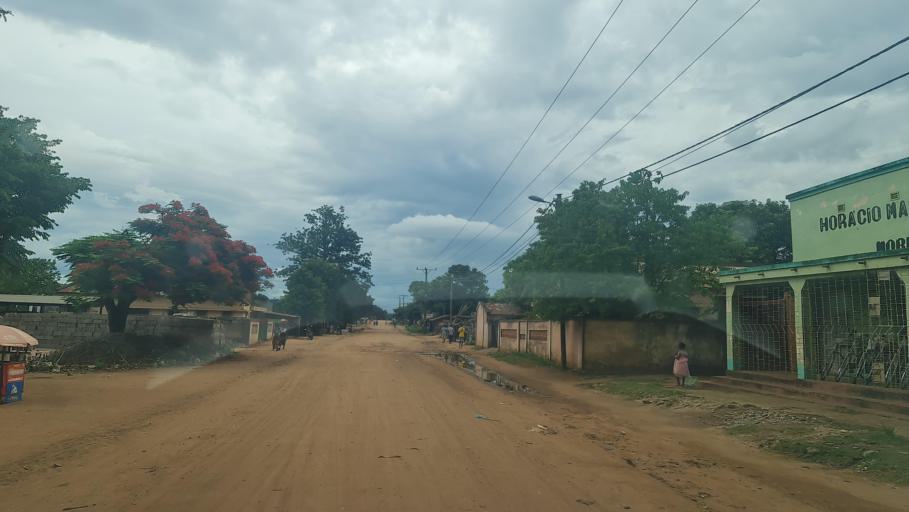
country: MW
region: Southern Region
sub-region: Nsanje District
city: Nsanje
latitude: -17.3325
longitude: 35.5955
